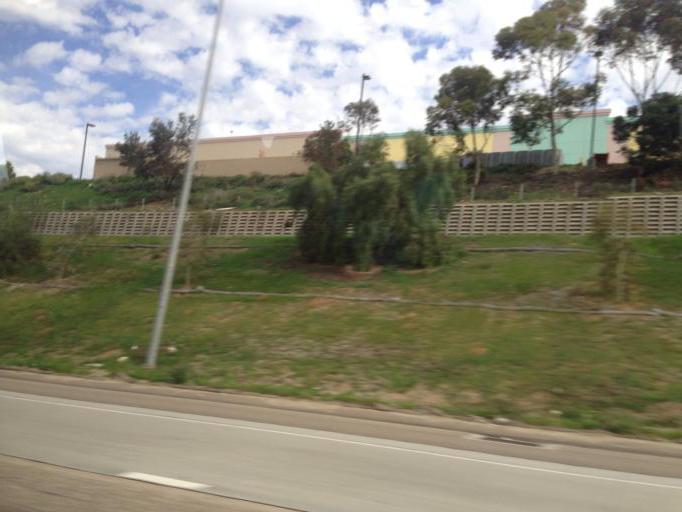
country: US
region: California
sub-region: San Diego County
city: Imperial Beach
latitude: 32.5765
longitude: -117.0385
